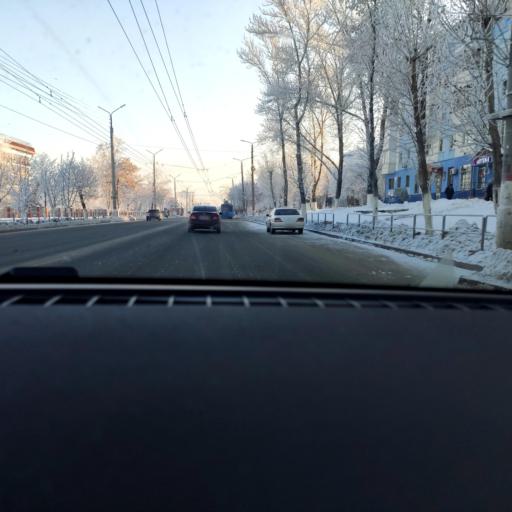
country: RU
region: Samara
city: Novokuybyshevsk
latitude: 53.0999
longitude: 49.9609
